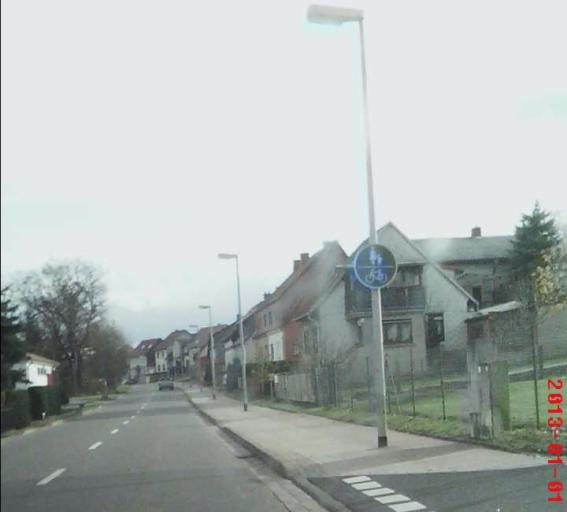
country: DE
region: Thuringia
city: Anrode
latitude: 51.2520
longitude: 10.3432
